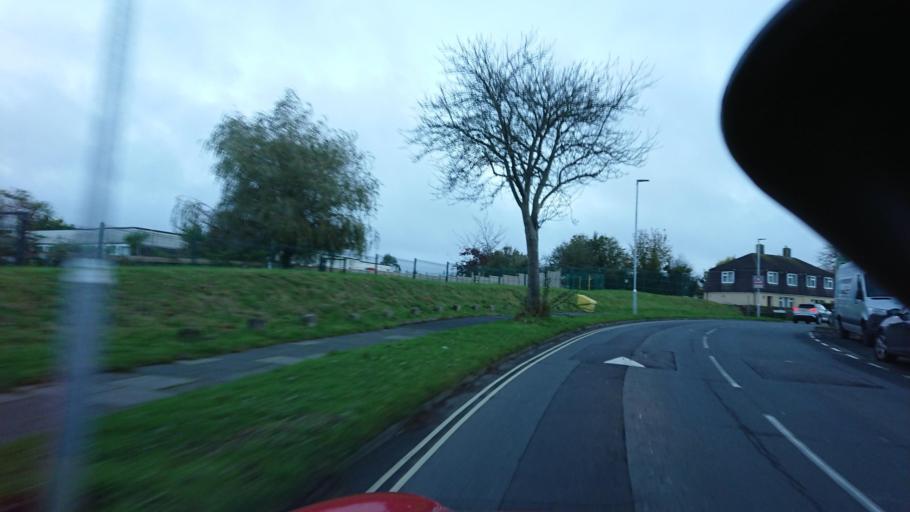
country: GB
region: England
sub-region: Cornwall
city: Torpoint
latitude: 50.4180
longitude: -4.1712
